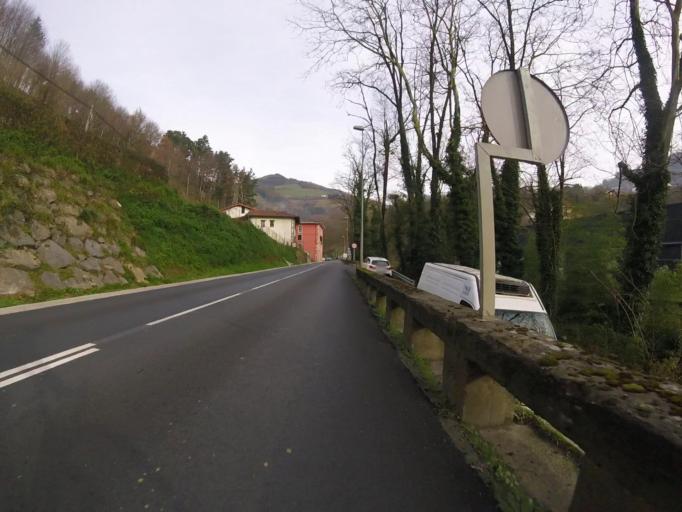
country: ES
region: Basque Country
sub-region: Provincia de Guipuzcoa
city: Belaunza
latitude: 43.1346
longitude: -2.0579
